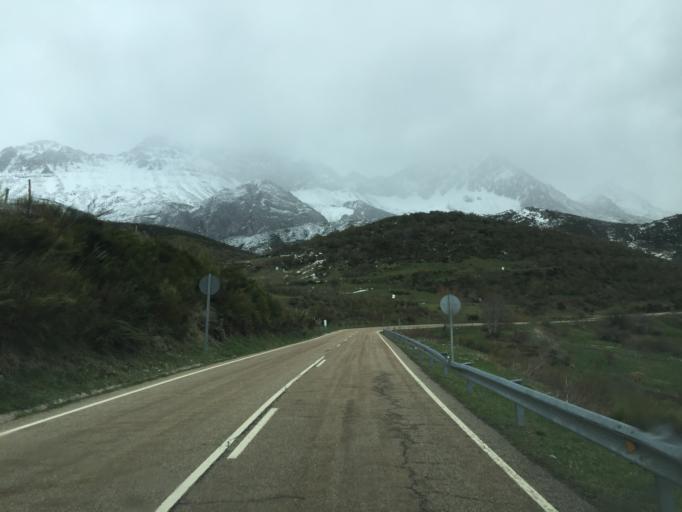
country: ES
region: Castille and Leon
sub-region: Provincia de Leon
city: San Emiliano
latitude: 43.0319
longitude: -6.0107
